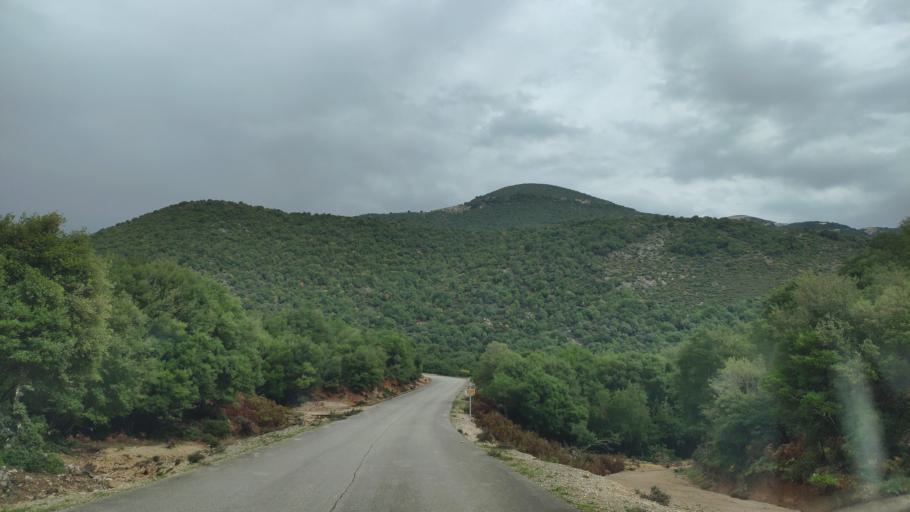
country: GR
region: Epirus
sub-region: Nomos Thesprotias
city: Paramythia
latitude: 39.4091
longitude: 20.6217
